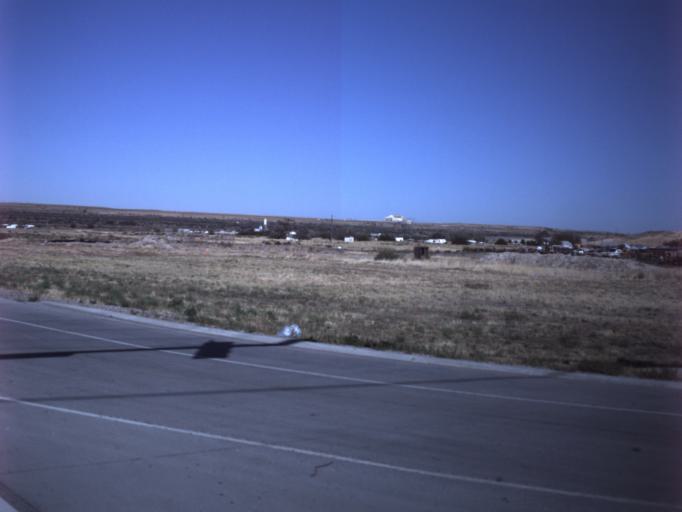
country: US
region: Utah
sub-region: Salt Lake County
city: Magna
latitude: 40.7188
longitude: -112.0631
